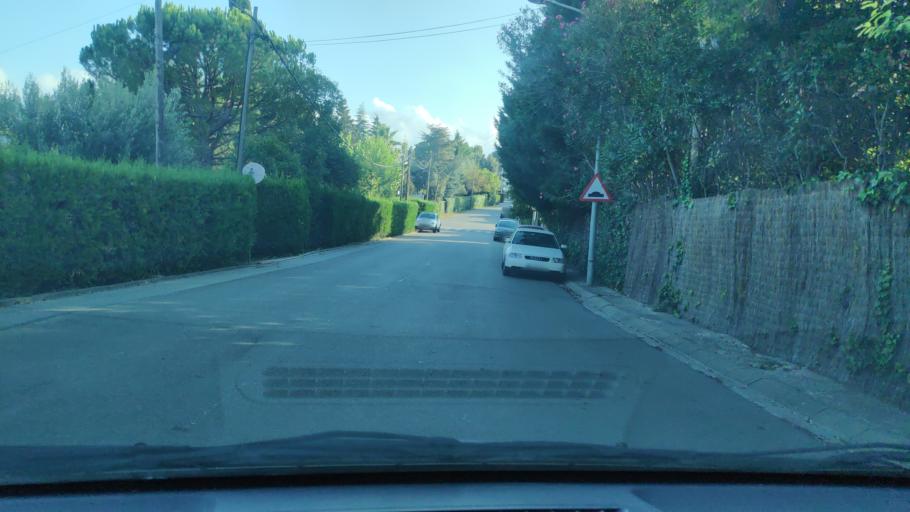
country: ES
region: Catalonia
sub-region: Provincia de Barcelona
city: Sant Quirze del Valles
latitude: 41.5010
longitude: 2.0801
